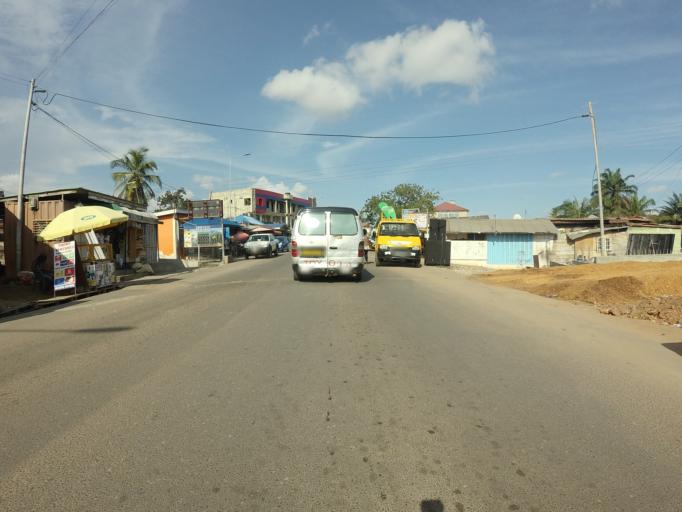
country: GH
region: Greater Accra
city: Medina Estates
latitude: 5.6420
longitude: -0.1655
